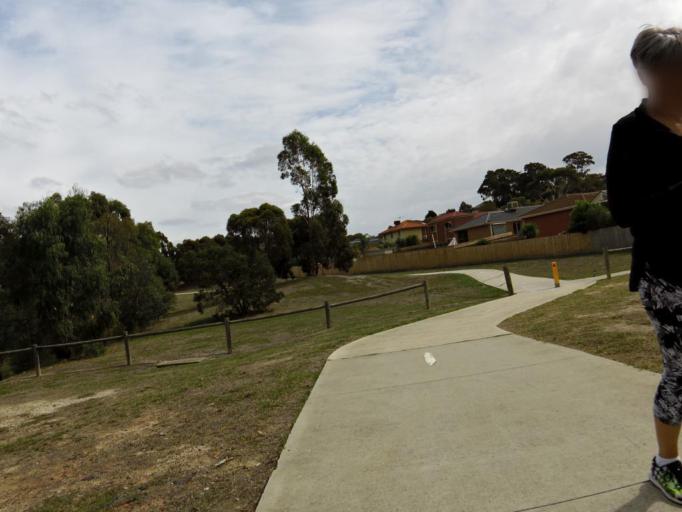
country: AU
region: Victoria
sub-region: Hume
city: Sunbury
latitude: -37.5684
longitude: 144.7120
